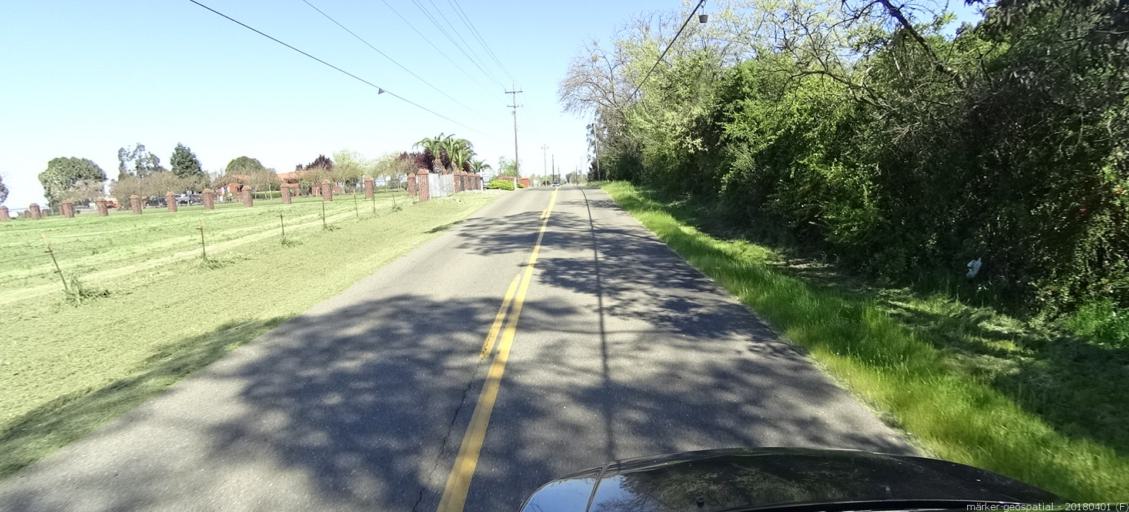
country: US
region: California
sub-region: Sacramento County
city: Wilton
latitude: 38.3735
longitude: -121.2421
